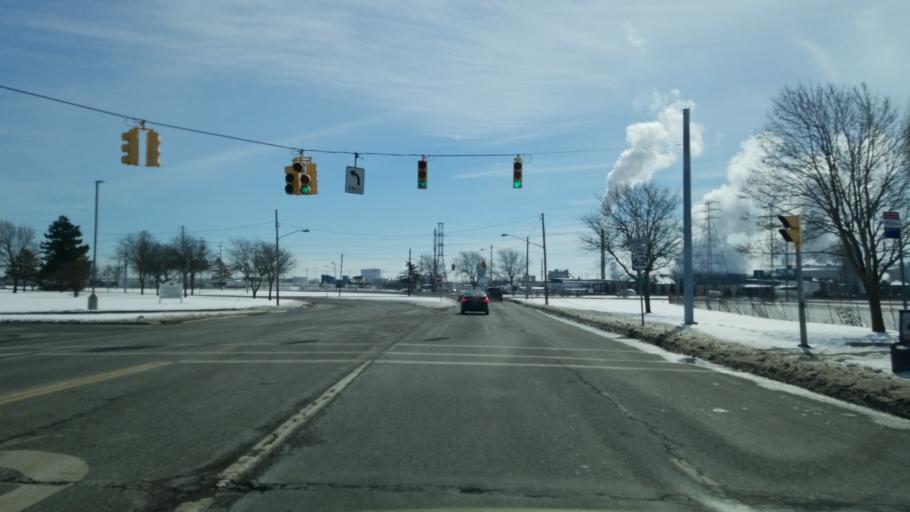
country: US
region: New York
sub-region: Niagara County
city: Niagara Falls
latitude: 43.0946
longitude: -79.0160
